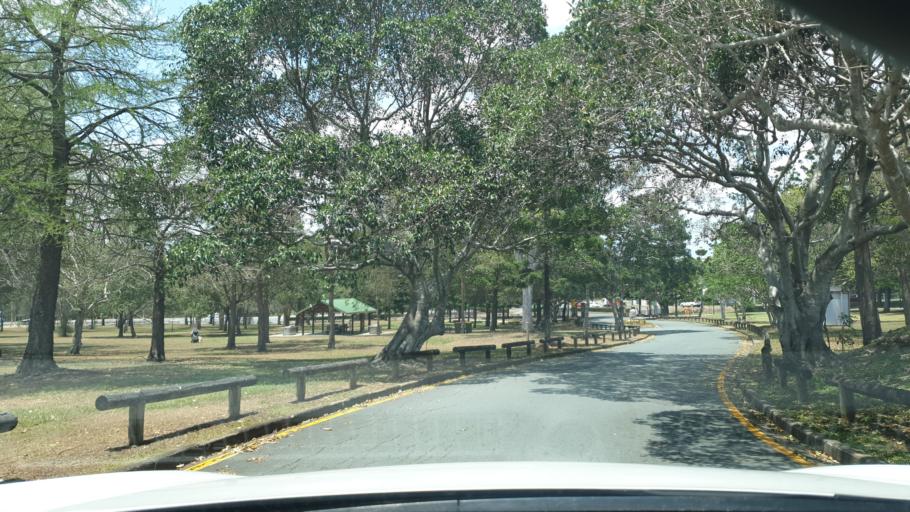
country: AU
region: Queensland
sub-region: Brisbane
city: Chermside West
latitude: -27.3772
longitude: 153.0297
